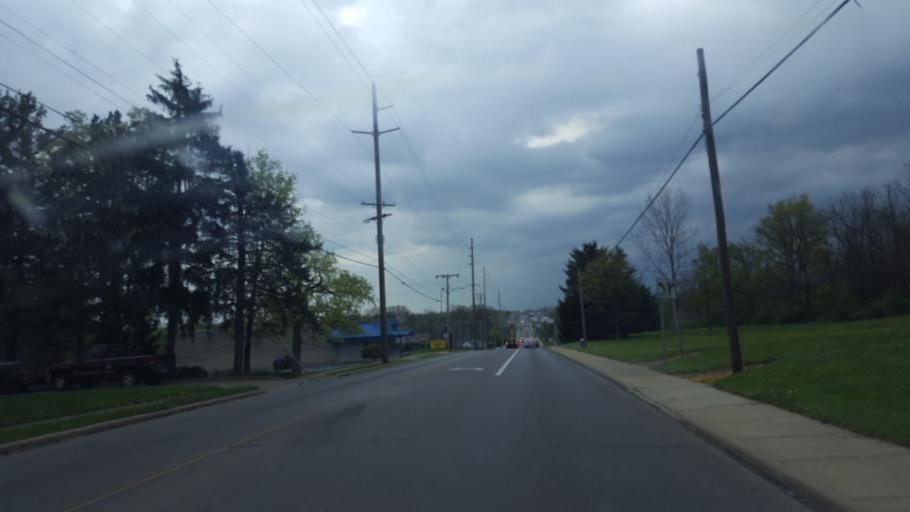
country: US
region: Ohio
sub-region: Richland County
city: Mansfield
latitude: 40.7574
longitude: -82.5517
